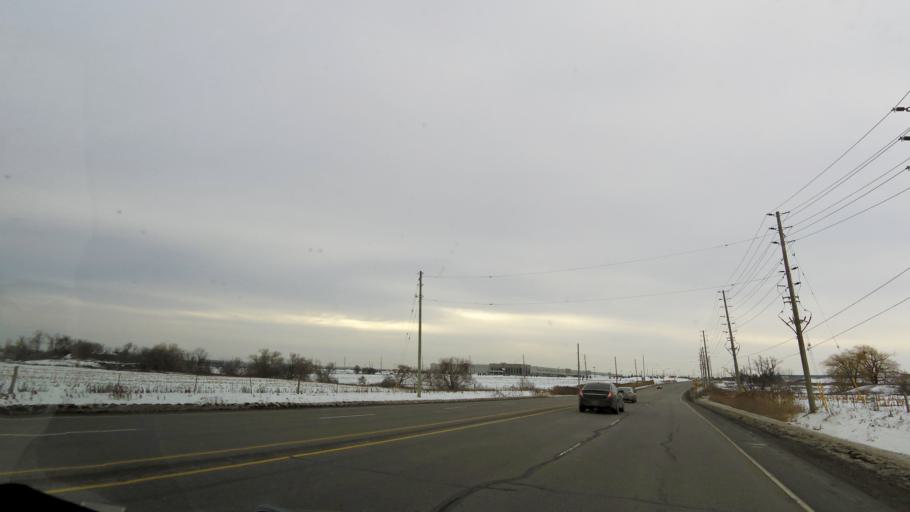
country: CA
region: Ontario
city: Vaughan
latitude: 43.8054
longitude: -79.6506
